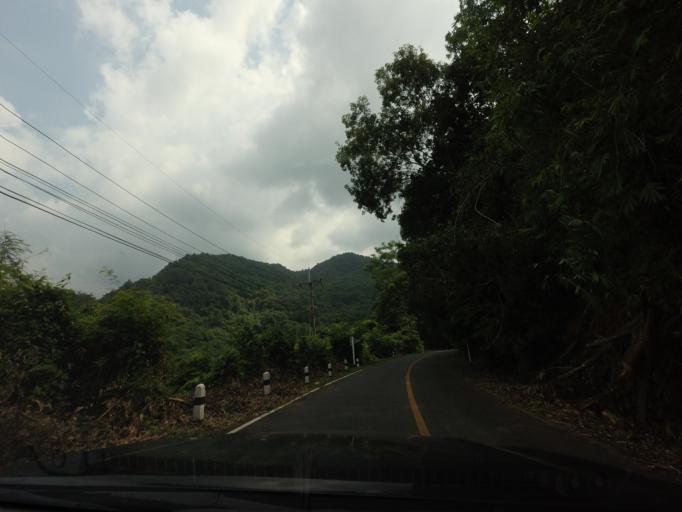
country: TH
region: Nan
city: Pua
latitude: 19.1815
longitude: 100.9757
